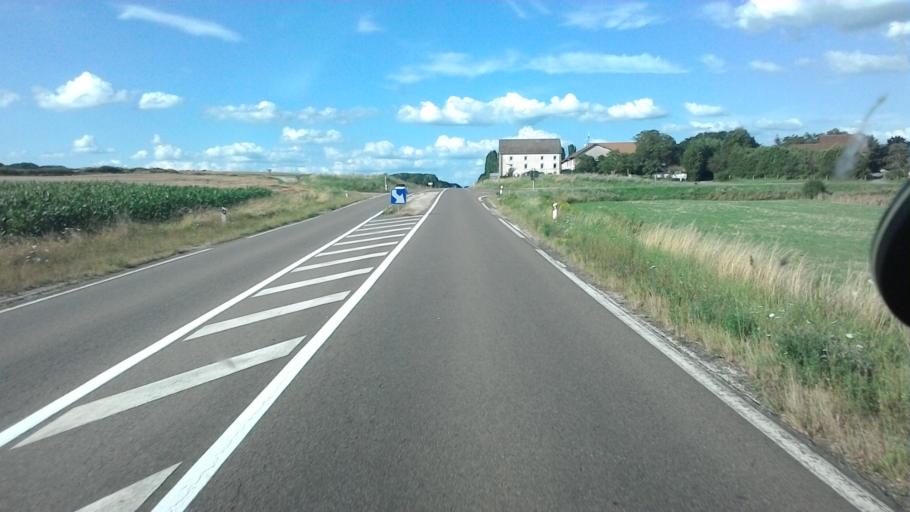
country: FR
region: Franche-Comte
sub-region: Departement de la Haute-Saone
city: Luxeuil-les-Bains
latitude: 47.7308
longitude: 6.3132
